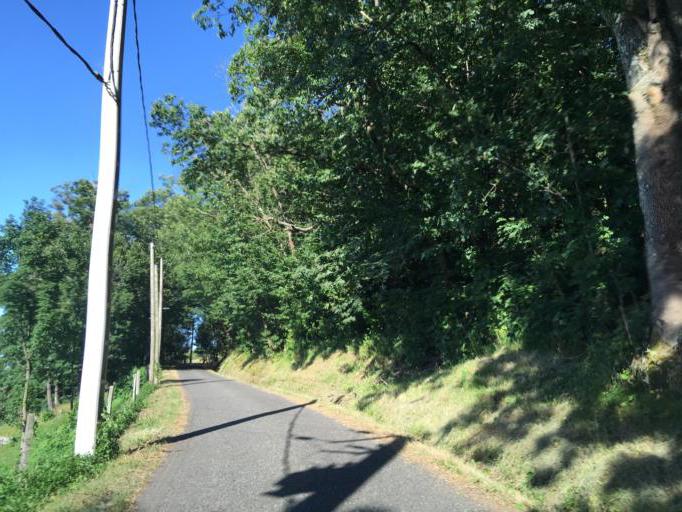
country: FR
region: Rhone-Alpes
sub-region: Departement de la Loire
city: Saint-Jean-Bonnefonds
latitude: 45.4316
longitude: 4.4703
